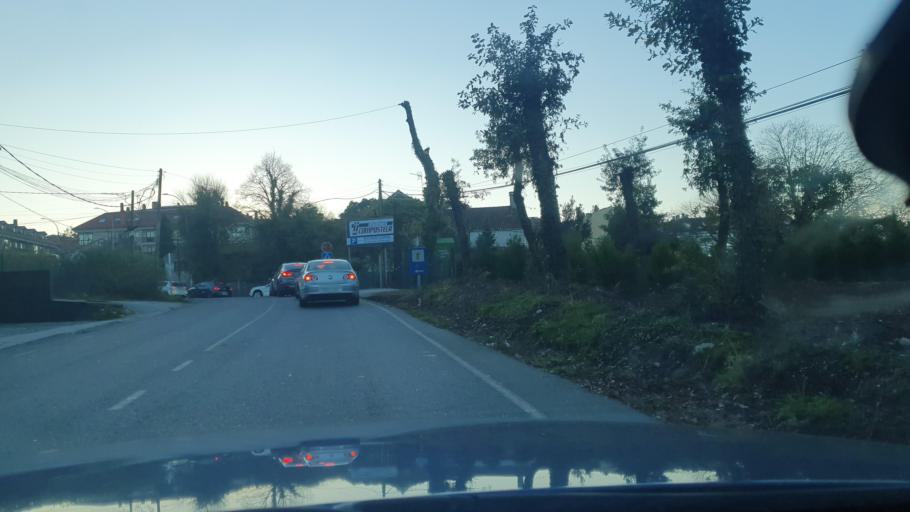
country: ES
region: Galicia
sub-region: Provincia da Coruna
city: Santiago de Compostela
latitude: 42.8434
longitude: -8.5825
